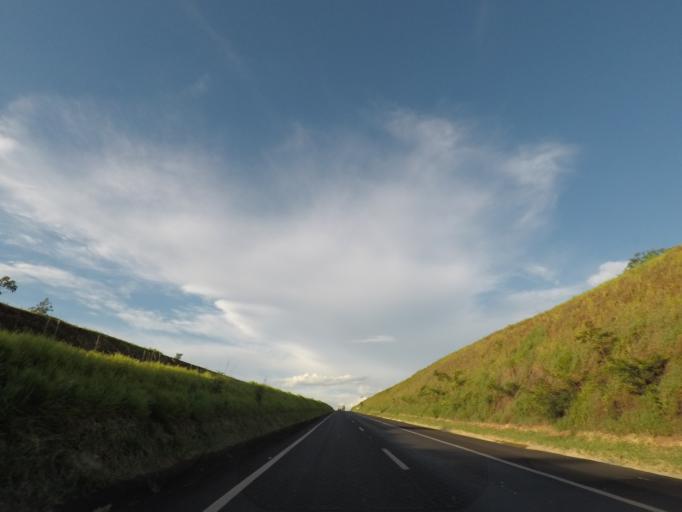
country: BR
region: Sao Paulo
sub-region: Ituverava
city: Ituverava
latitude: -20.2501
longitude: -47.7990
